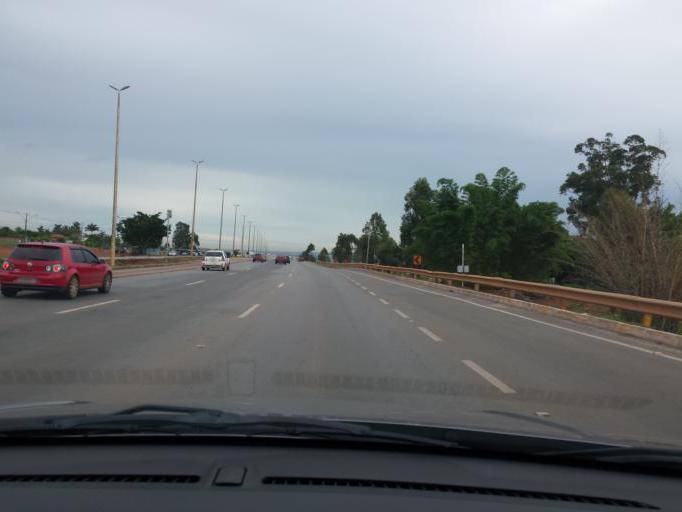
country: BR
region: Federal District
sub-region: Brasilia
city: Brasilia
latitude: -15.9041
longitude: -47.9634
